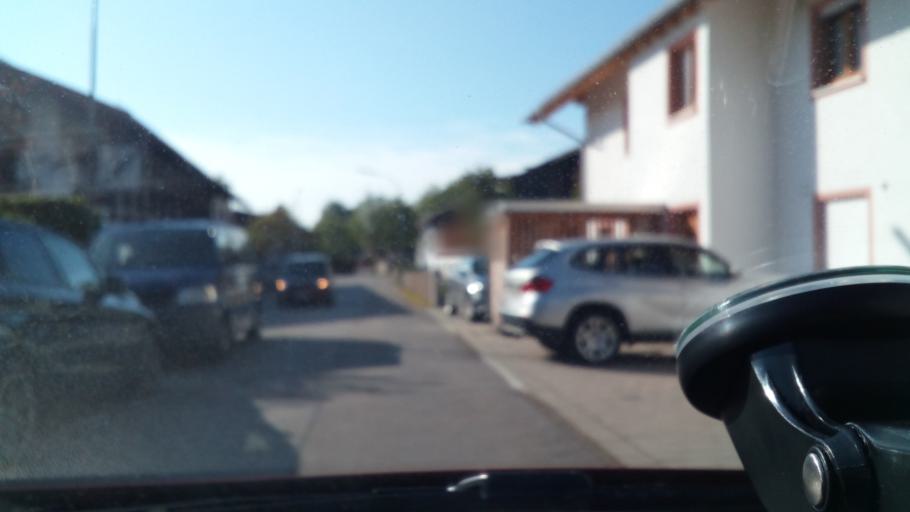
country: DE
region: Bavaria
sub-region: Upper Bavaria
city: Holzkirchen
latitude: 47.8749
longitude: 11.6971
